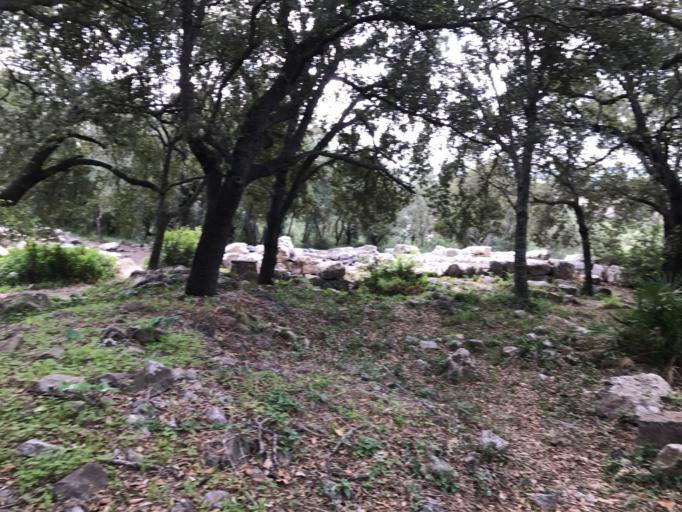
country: ES
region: Balearic Islands
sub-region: Illes Balears
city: Arta
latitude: 39.6875
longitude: 3.3531
